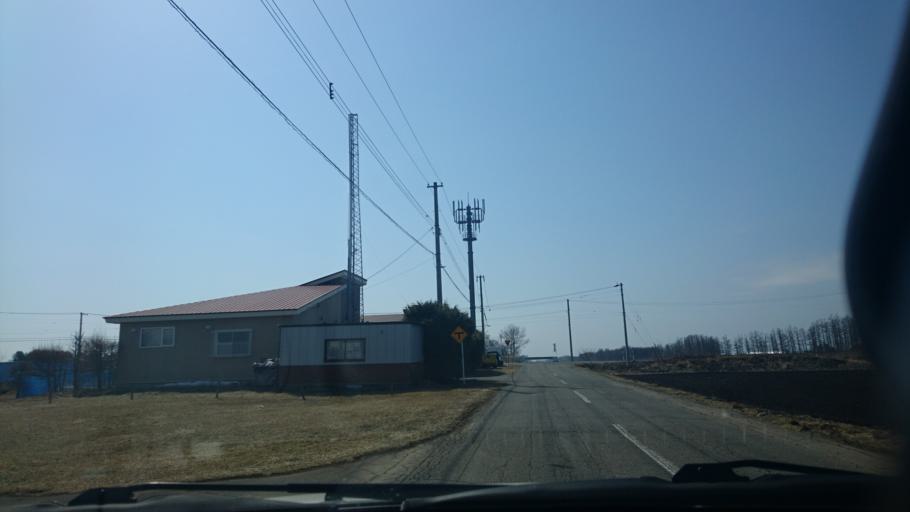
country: JP
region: Hokkaido
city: Otofuke
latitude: 43.0934
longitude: 143.2254
